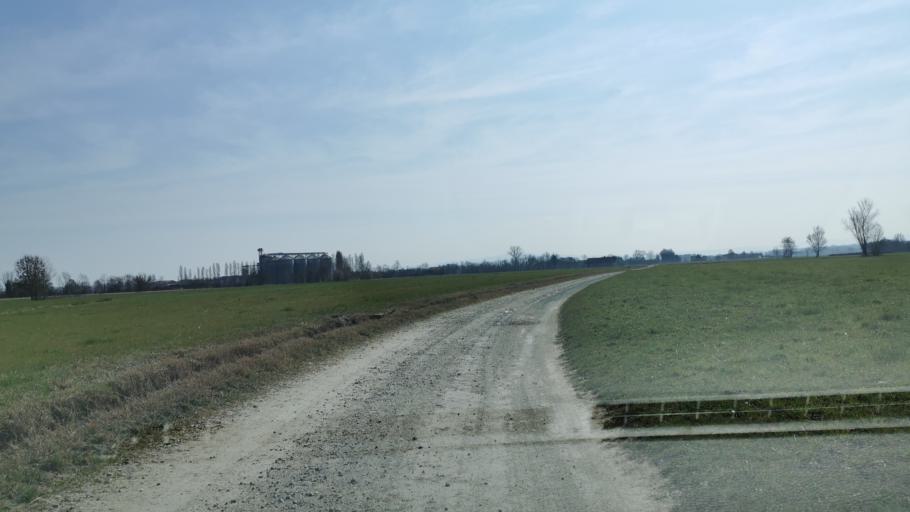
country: IT
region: Piedmont
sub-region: Provincia di Torino
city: Feletto
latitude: 45.2844
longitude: 7.7152
